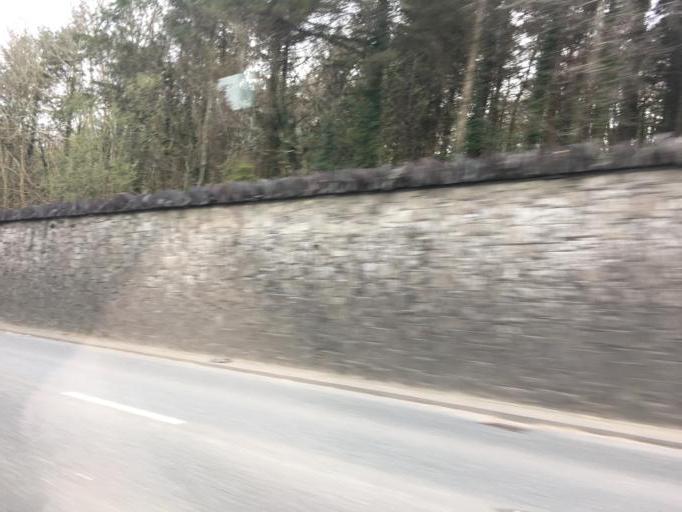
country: GB
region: Wales
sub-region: Gwynedd
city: Y Felinheli
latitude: 53.1985
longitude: -4.1818
